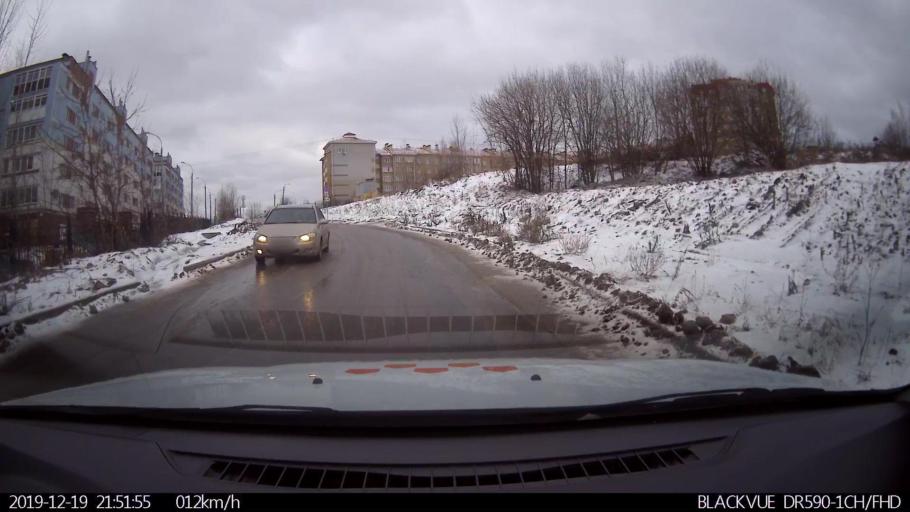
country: RU
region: Nizjnij Novgorod
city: Afonino
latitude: 56.2825
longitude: 44.0832
